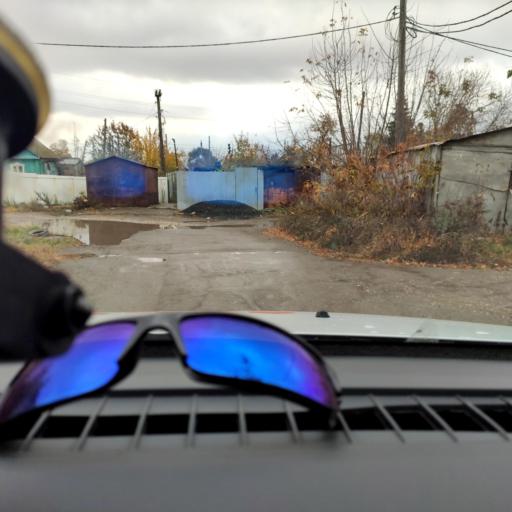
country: RU
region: Samara
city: Samara
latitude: 53.1720
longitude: 50.1761
